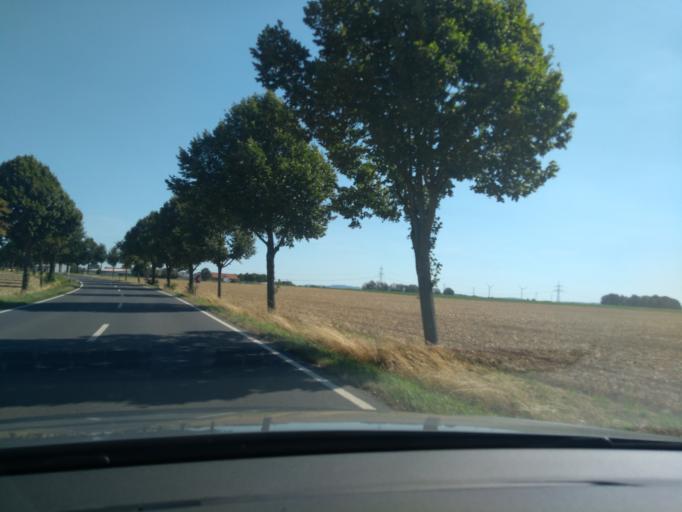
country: DE
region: Saxony
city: Crostwitz
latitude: 51.2218
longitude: 14.2260
